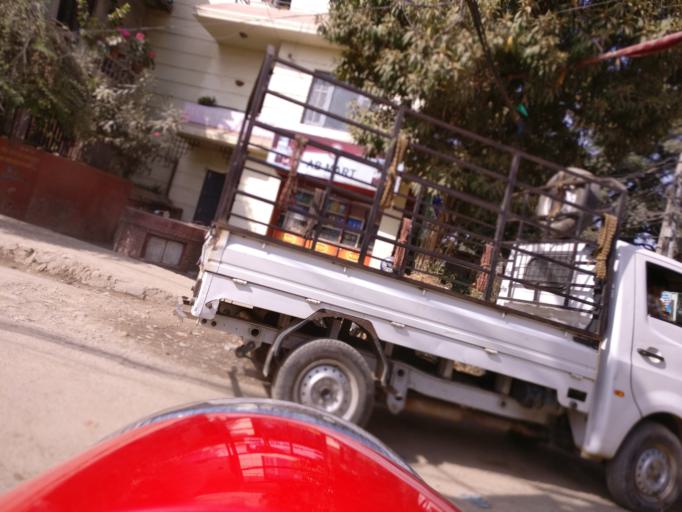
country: NP
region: Central Region
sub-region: Bagmati Zone
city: Patan
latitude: 27.6624
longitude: 85.3163
